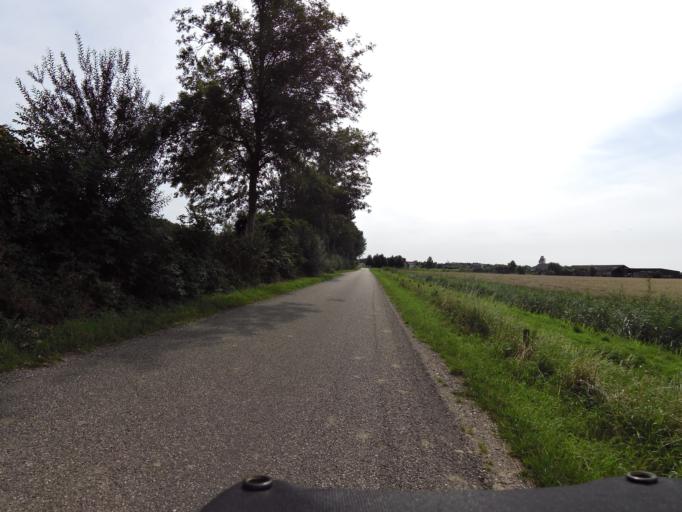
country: NL
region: South Holland
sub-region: Gemeente Goeree-Overflakkee
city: Middelharnis
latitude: 51.7637
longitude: 4.1715
